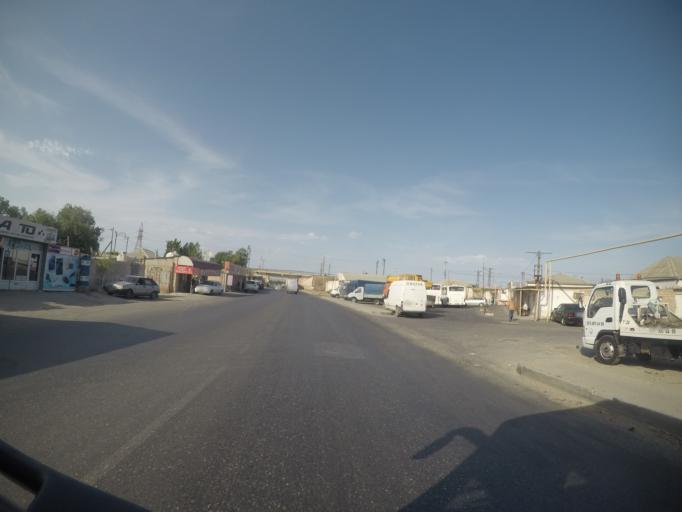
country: AZ
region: Baki
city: Bilajari
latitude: 40.4409
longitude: 49.7849
